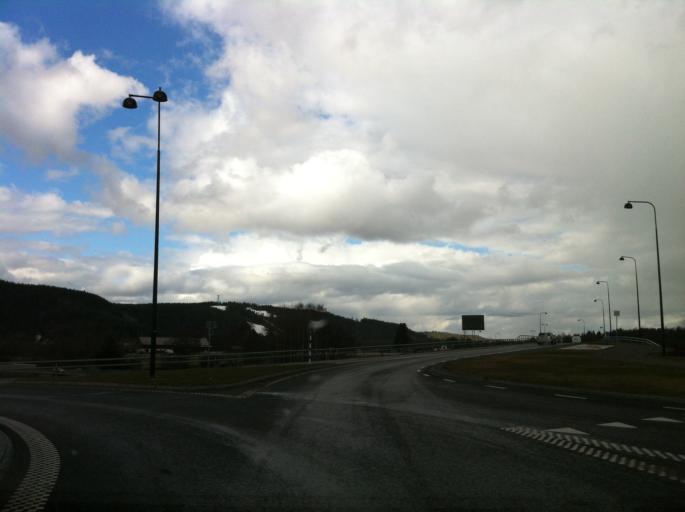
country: SE
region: Vaestra Goetaland
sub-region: Ulricehamns Kommun
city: Ulricehamn
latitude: 57.7419
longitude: 13.4316
